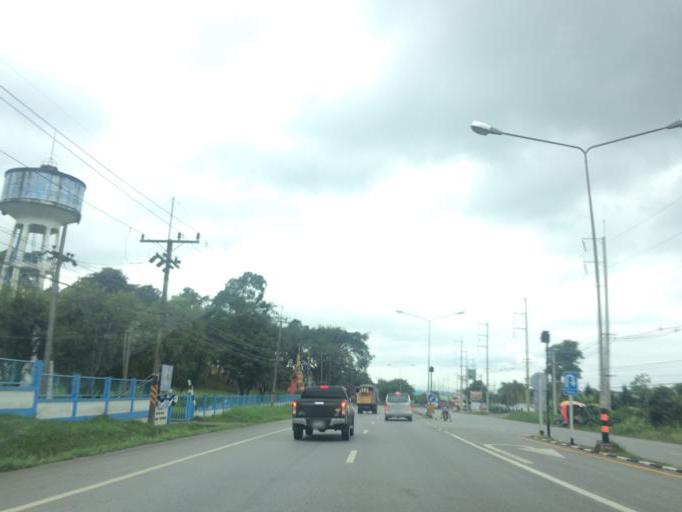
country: TH
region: Chiang Rai
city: Mae Chan
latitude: 20.1284
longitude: 99.8656
